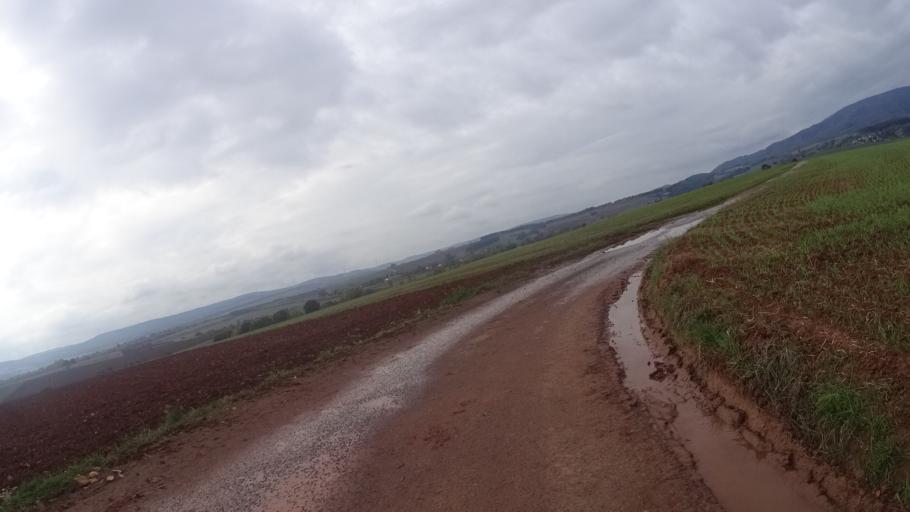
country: DE
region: Rheinland-Pfalz
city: Weitersweiler
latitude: 49.6260
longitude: 8.0090
